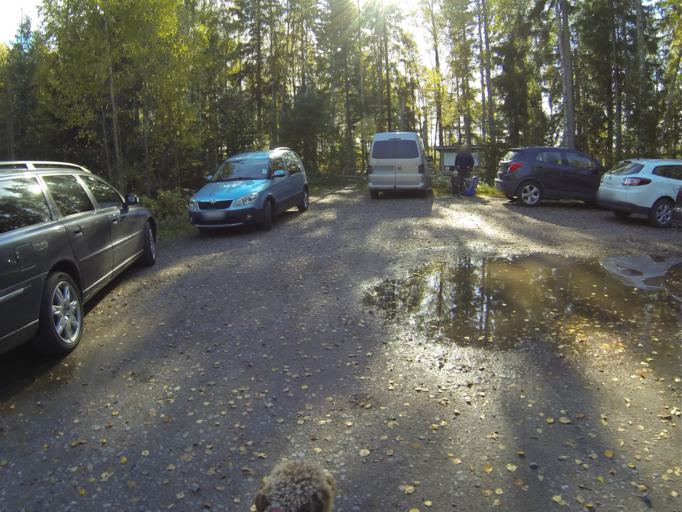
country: FI
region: Haeme
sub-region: Forssa
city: Forssa
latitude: 60.7370
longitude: 23.5763
